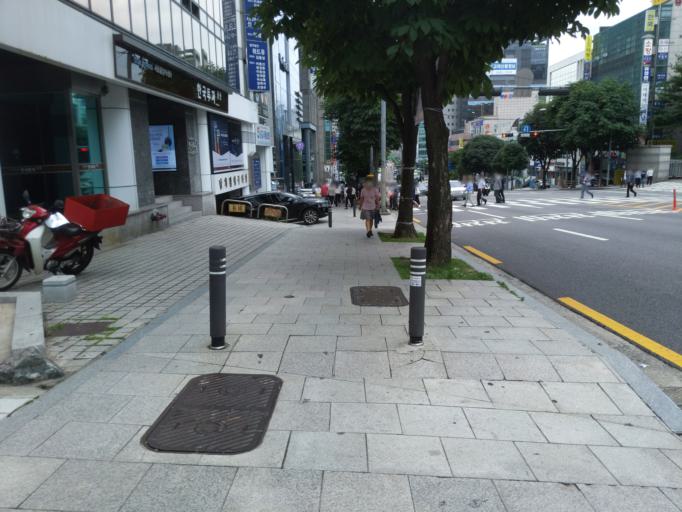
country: KR
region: Seoul
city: Seoul
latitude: 37.4961
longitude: 127.0132
